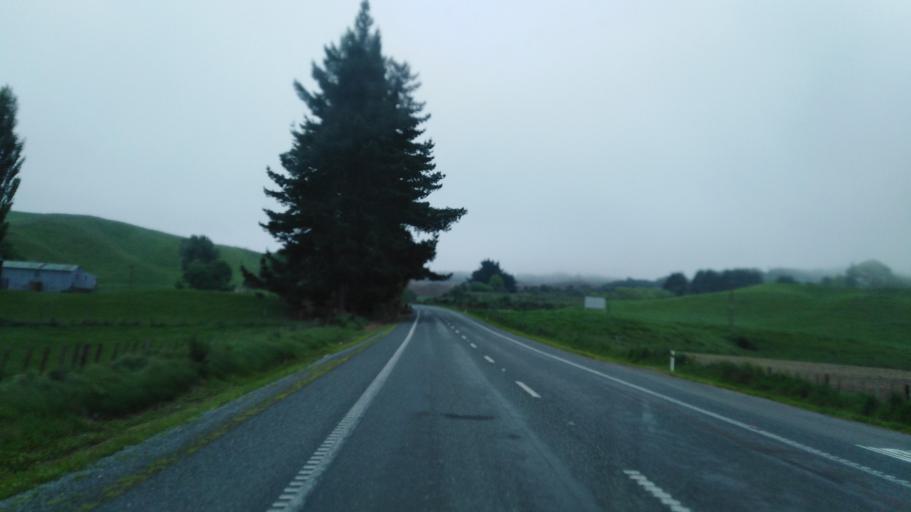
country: NZ
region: Bay of Plenty
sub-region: Rotorua District
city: Rotorua
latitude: -38.2755
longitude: 176.3375
